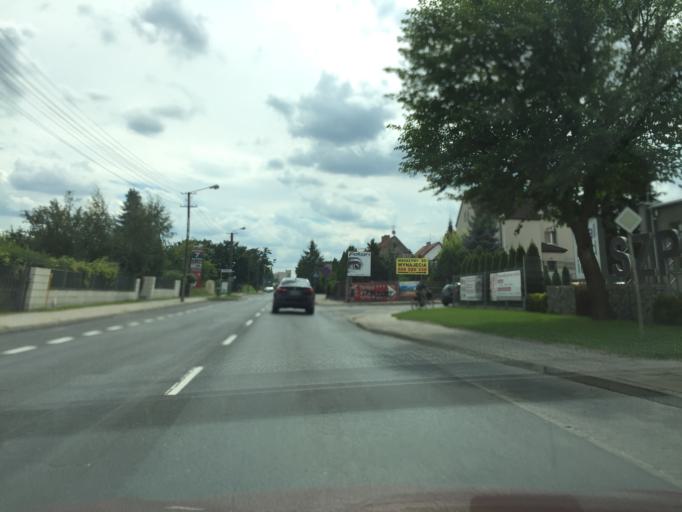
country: PL
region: Greater Poland Voivodeship
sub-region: Kalisz
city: Kalisz
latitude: 51.7468
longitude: 18.0965
